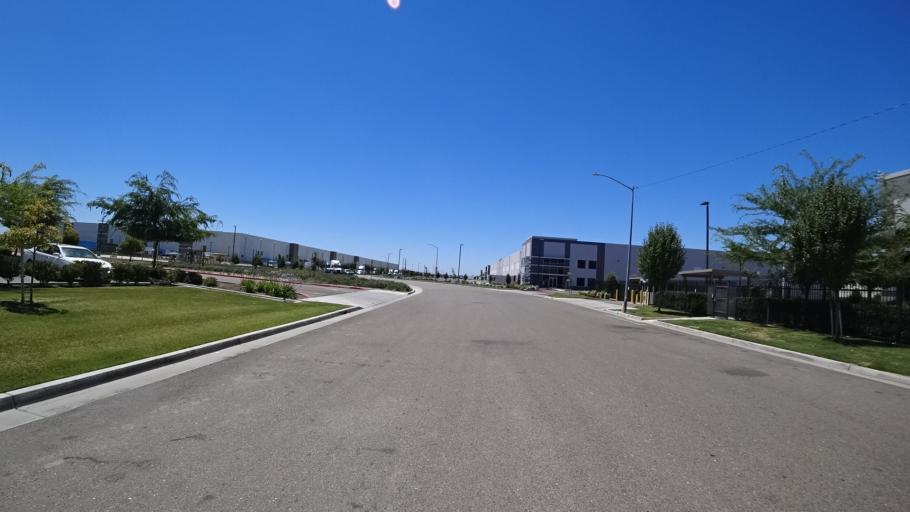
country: US
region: California
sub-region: Fresno County
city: Easton
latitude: 36.6873
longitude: -119.7680
